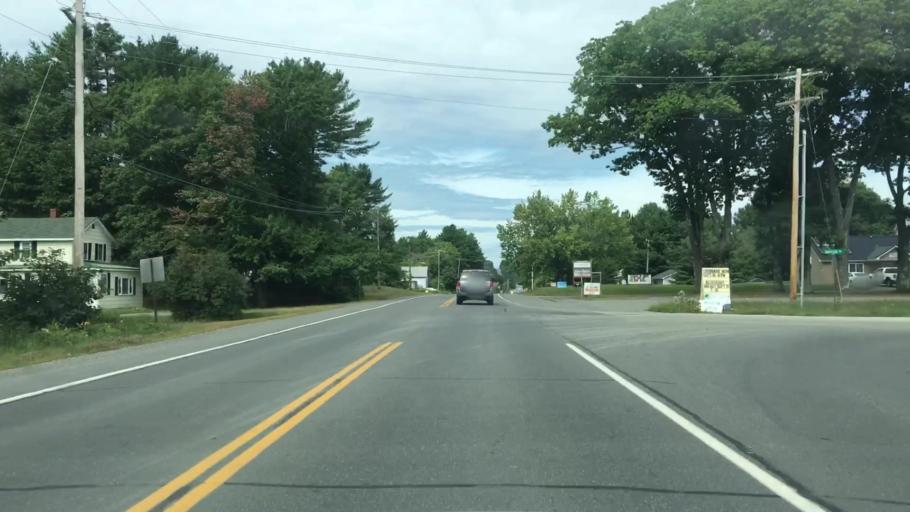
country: US
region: Maine
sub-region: Piscataquis County
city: Milo
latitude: 45.2658
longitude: -68.9936
